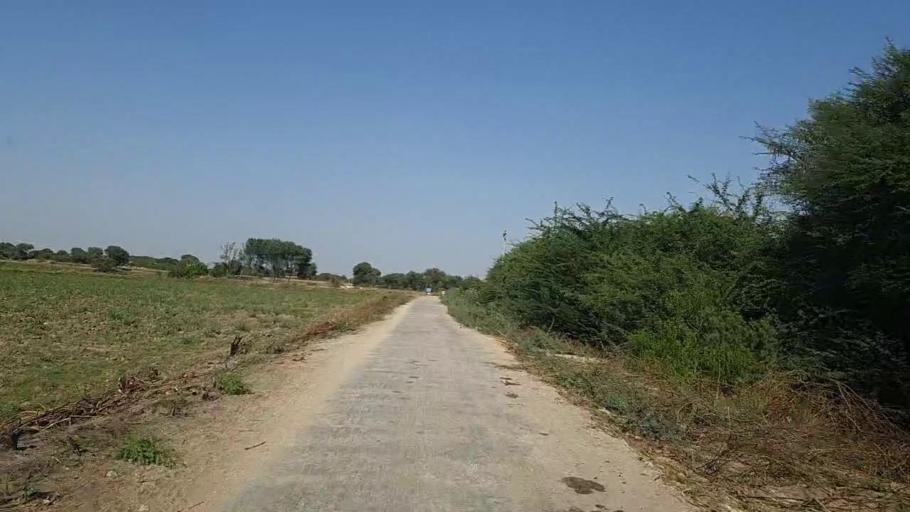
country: PK
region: Sindh
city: Kotri
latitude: 25.1738
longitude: 68.3039
